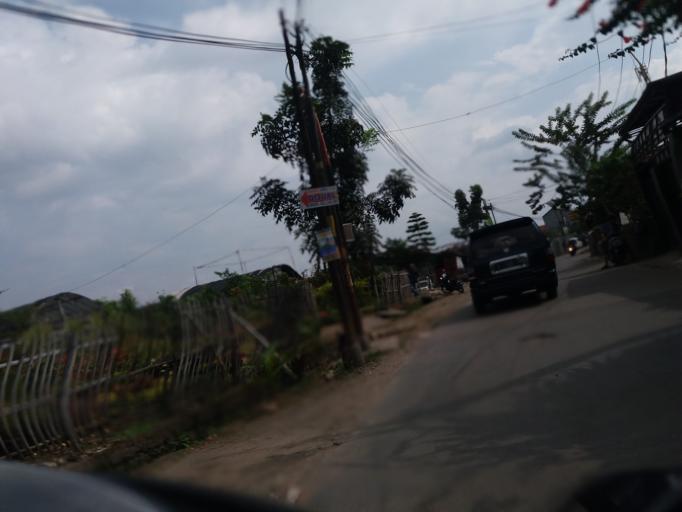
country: ID
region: West Java
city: Bandung
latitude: -6.9275
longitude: 107.6590
